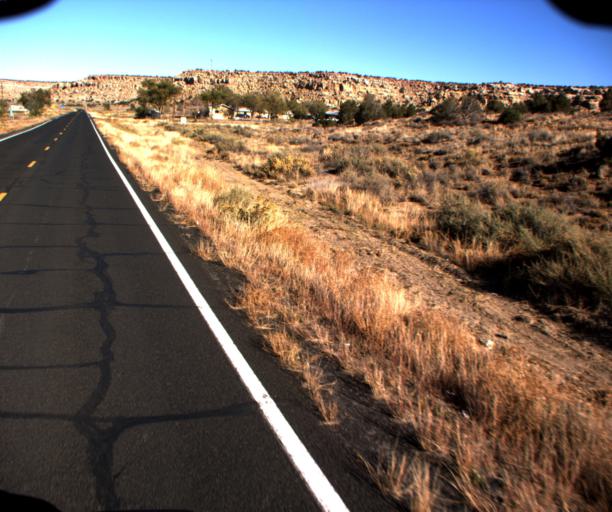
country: US
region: Arizona
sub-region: Navajo County
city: First Mesa
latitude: 35.8214
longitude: -110.2183
